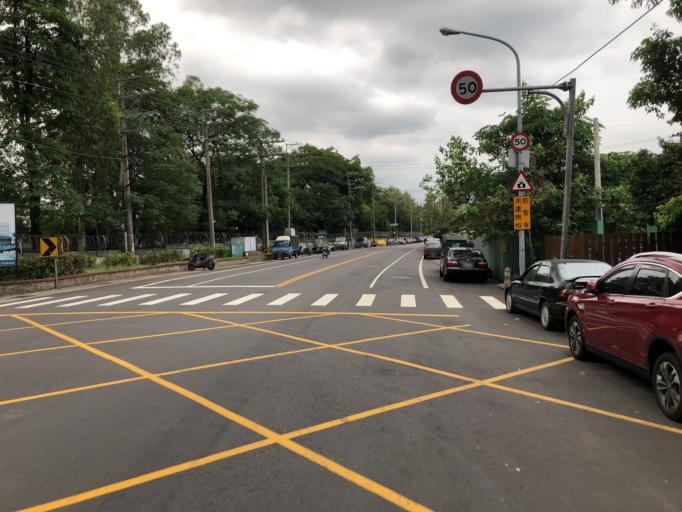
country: TW
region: Taiwan
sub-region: Taichung City
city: Taichung
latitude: 24.1157
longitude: 120.7324
